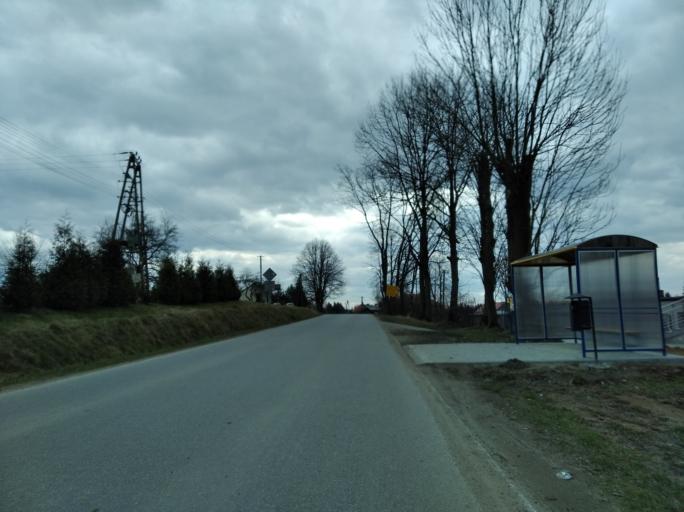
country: PL
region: Subcarpathian Voivodeship
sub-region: Powiat krosnienski
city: Odrzykon
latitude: 49.7570
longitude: 21.7166
